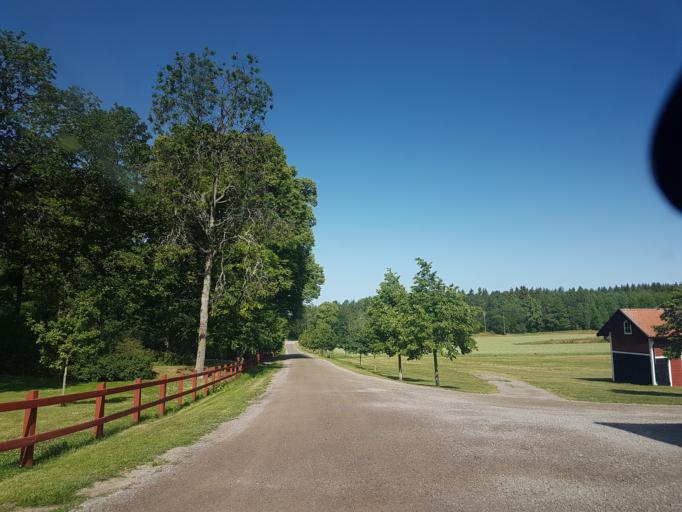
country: SE
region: OEstergoetland
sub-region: Norrkopings Kommun
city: Kimstad
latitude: 58.3825
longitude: 15.9479
